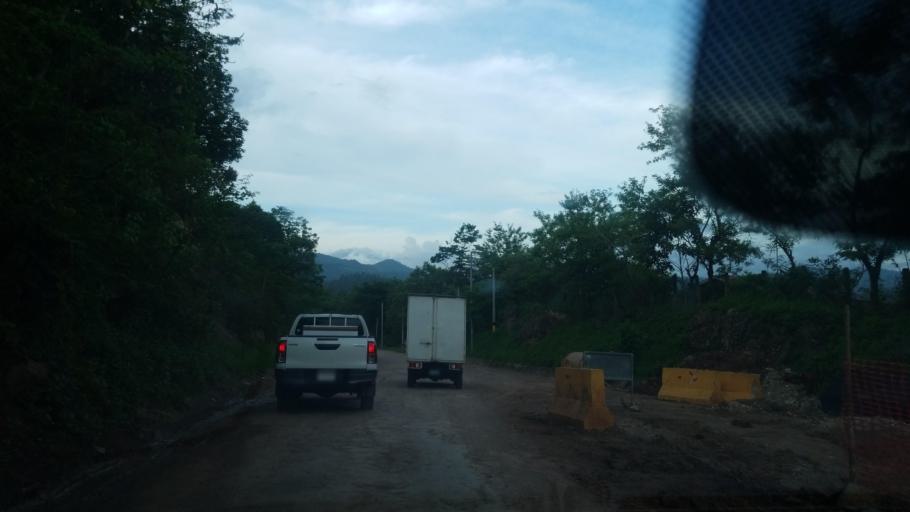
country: HN
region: Santa Barbara
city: Concepcion del Sur
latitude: 14.7988
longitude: -88.1504
